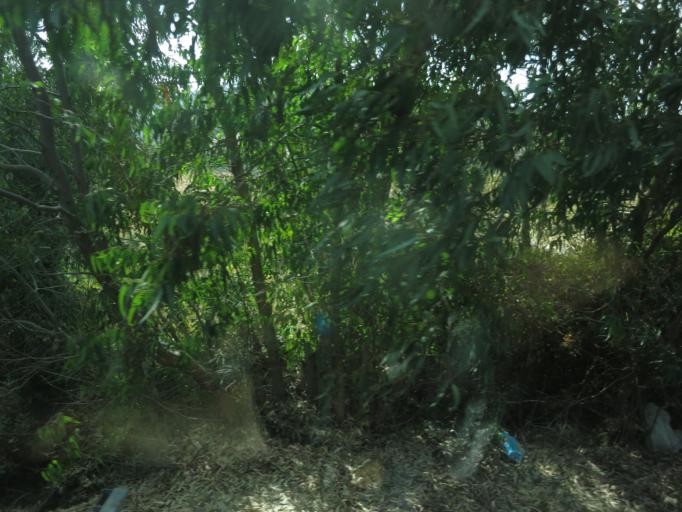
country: ES
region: Andalusia
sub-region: Provincia de Cadiz
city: Algeciras
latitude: 36.0848
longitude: -5.4954
